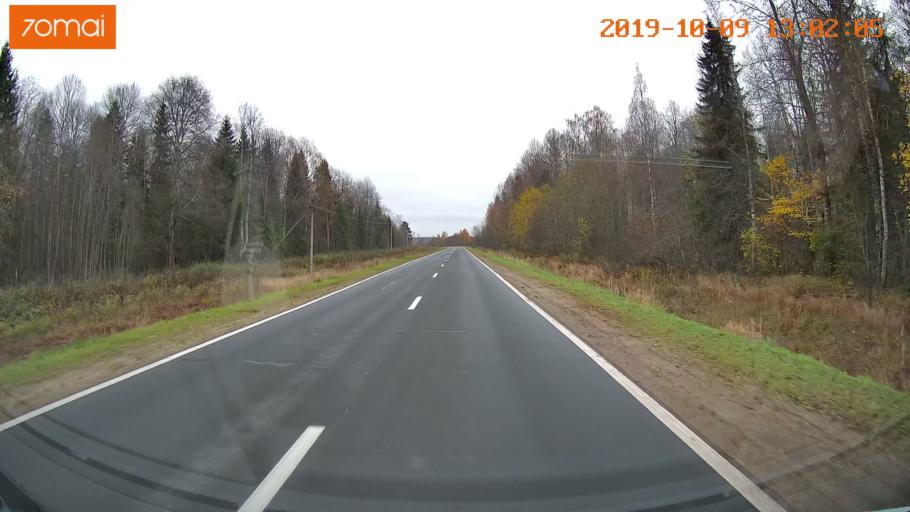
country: RU
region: Jaroslavl
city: Prechistoye
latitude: 58.3640
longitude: 40.4946
